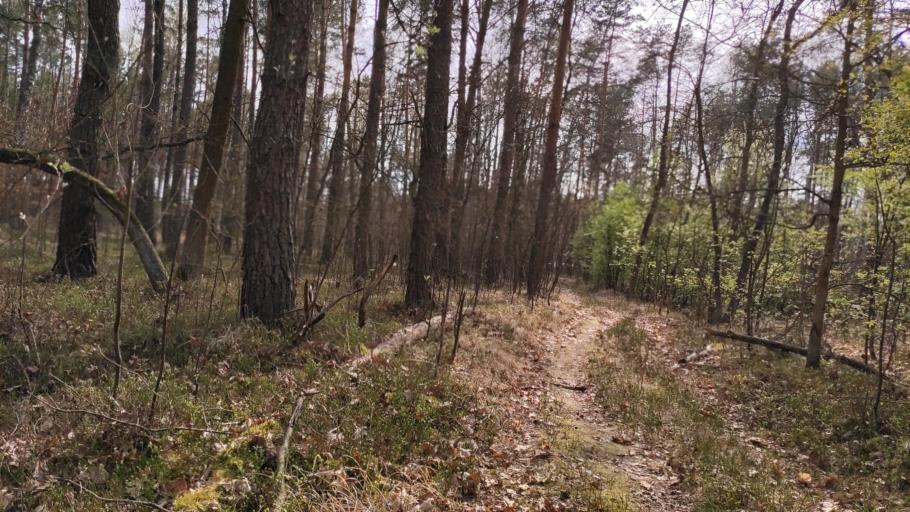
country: PL
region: Masovian Voivodeship
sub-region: Powiat grojecki
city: Warka
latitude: 51.7660
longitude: 21.1888
